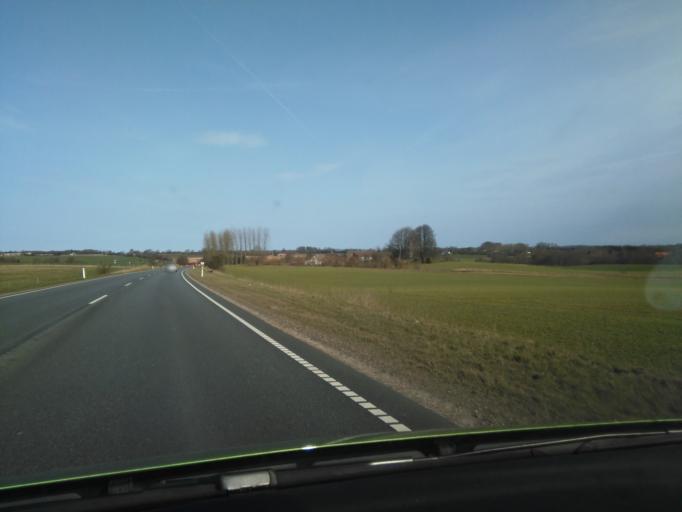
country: DK
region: Central Jutland
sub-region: Silkeborg Kommune
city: Kjellerup
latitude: 56.2921
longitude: 9.4169
